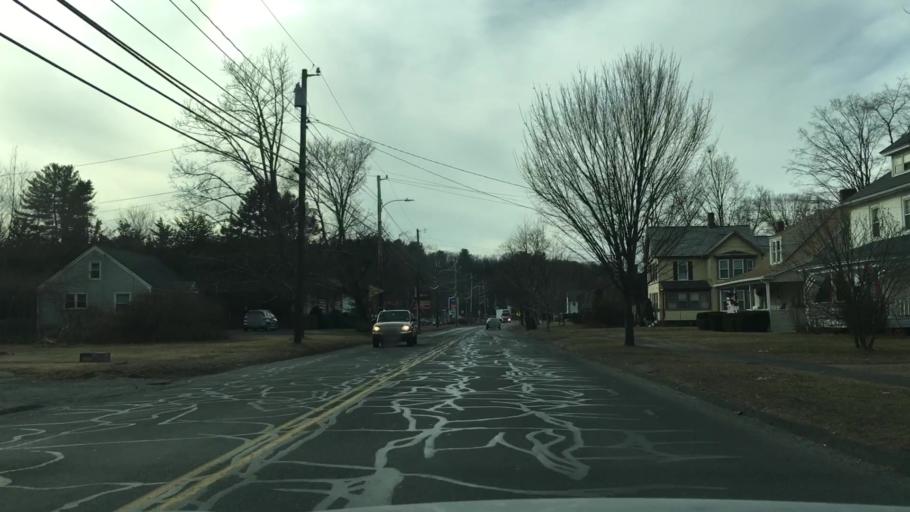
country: US
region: Massachusetts
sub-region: Hampden County
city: Westfield
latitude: 42.1120
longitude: -72.7607
